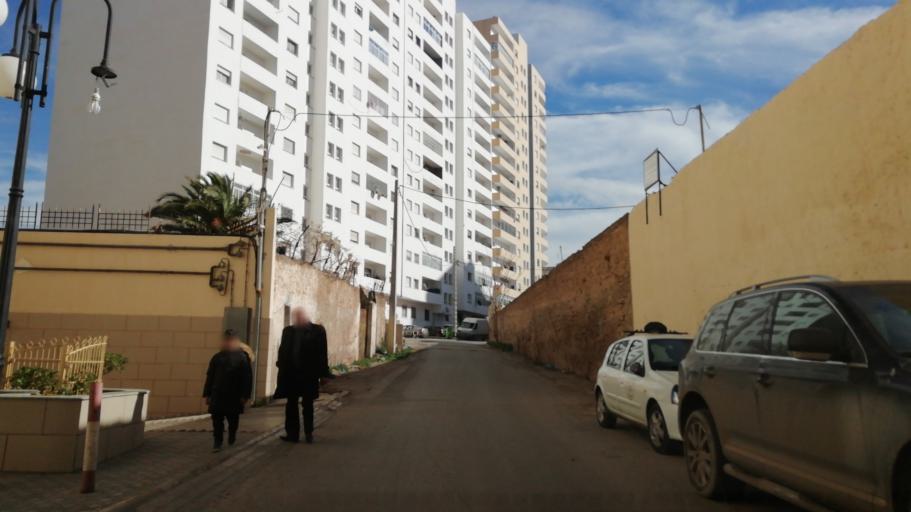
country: DZ
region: Oran
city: Oran
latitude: 35.7033
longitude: -0.6215
